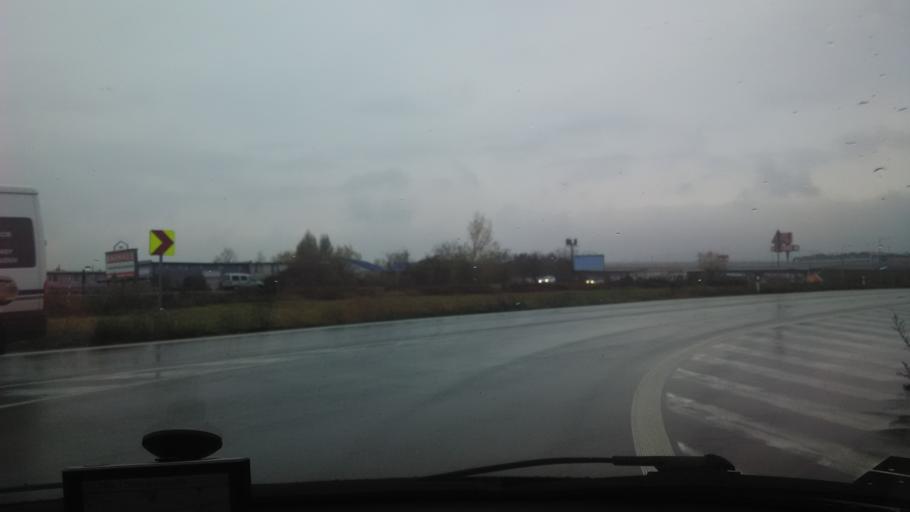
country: SK
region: Bratislavsky
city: Bratislava
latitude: 48.1592
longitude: 17.1890
